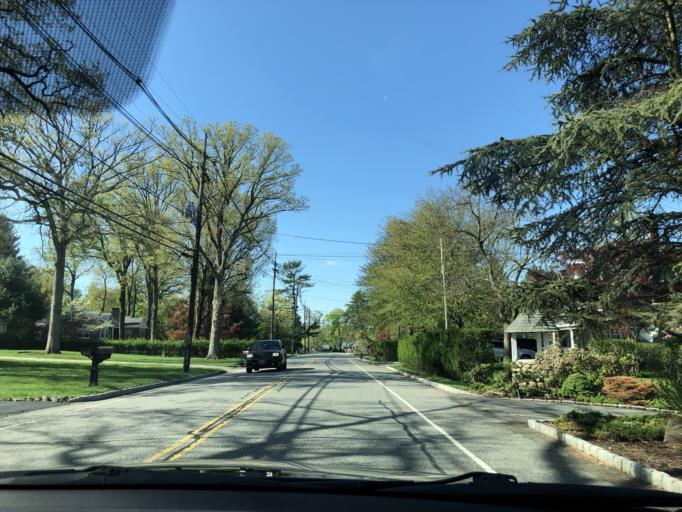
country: US
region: New Jersey
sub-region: Essex County
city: North Caldwell
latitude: 40.8742
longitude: -74.2602
